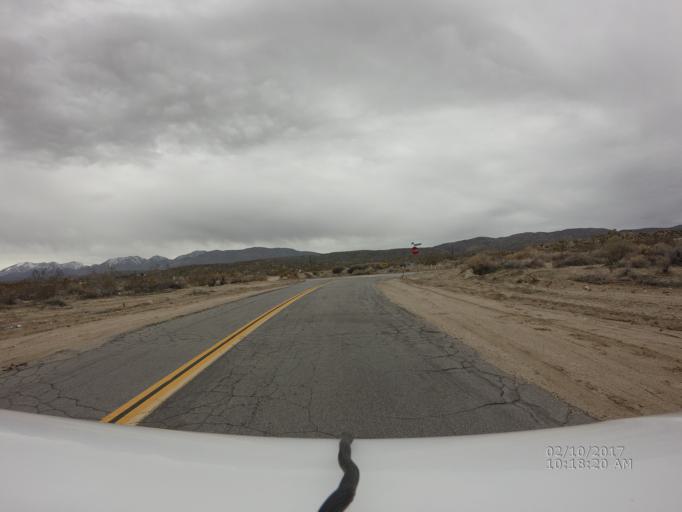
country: US
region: California
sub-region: Los Angeles County
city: Littlerock
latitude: 34.5011
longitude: -117.9580
